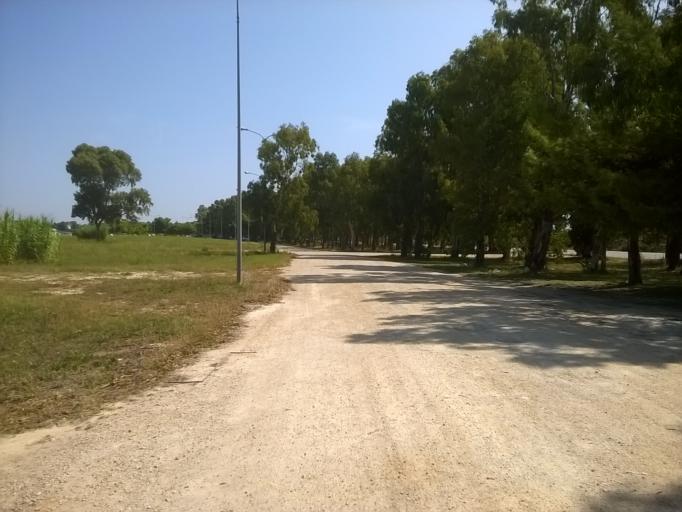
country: IT
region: Apulia
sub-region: Provincia di Taranto
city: Taranto
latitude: 40.4231
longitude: 17.2309
